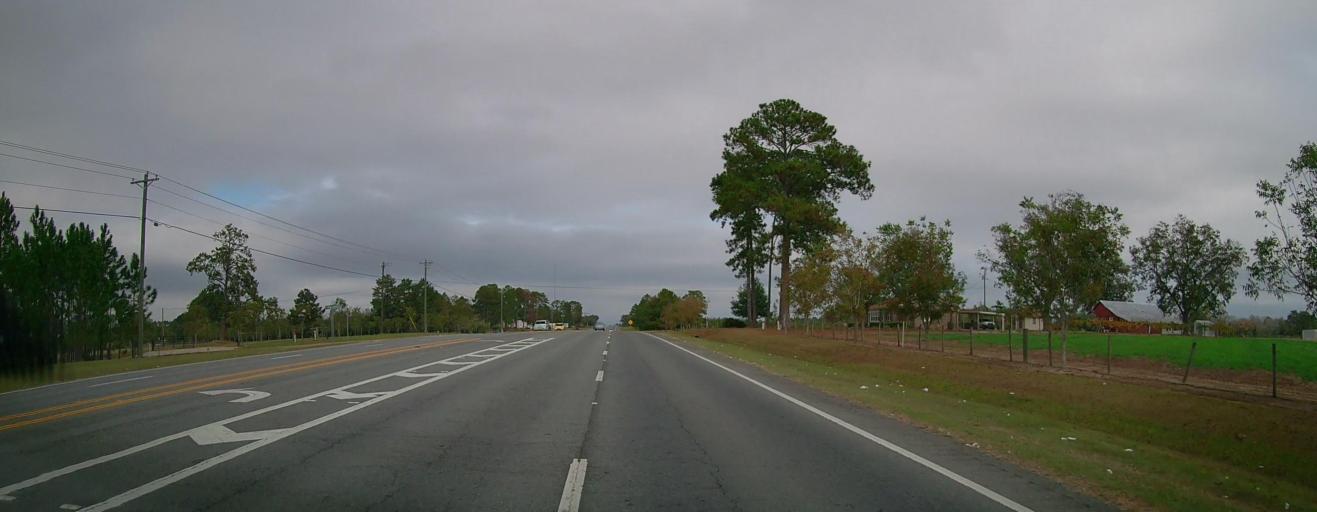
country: US
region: Georgia
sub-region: Tift County
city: Omega
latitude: 31.3544
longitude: -83.5828
